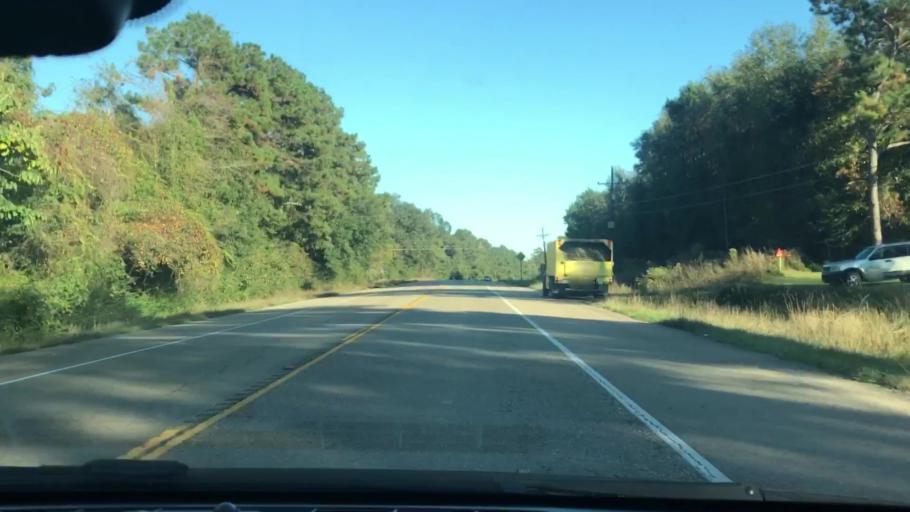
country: US
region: Louisiana
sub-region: Washington Parish
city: Bogalusa
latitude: 30.6088
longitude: -89.8834
